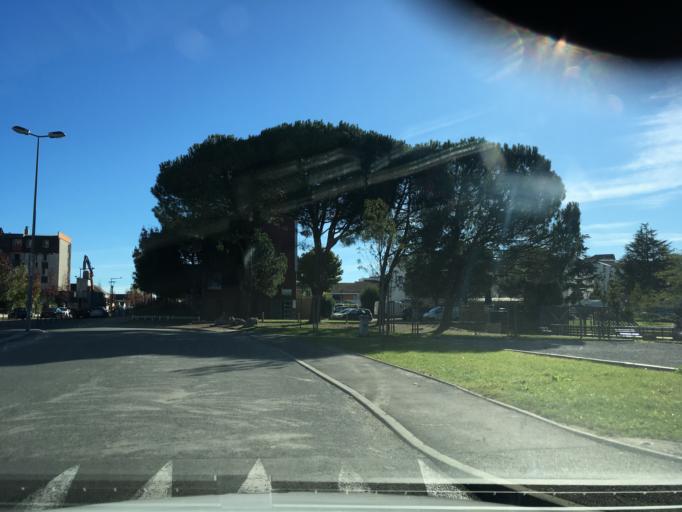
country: FR
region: Aquitaine
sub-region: Departement des Pyrenees-Atlantiques
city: Pau
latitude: 43.3204
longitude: -0.3439
